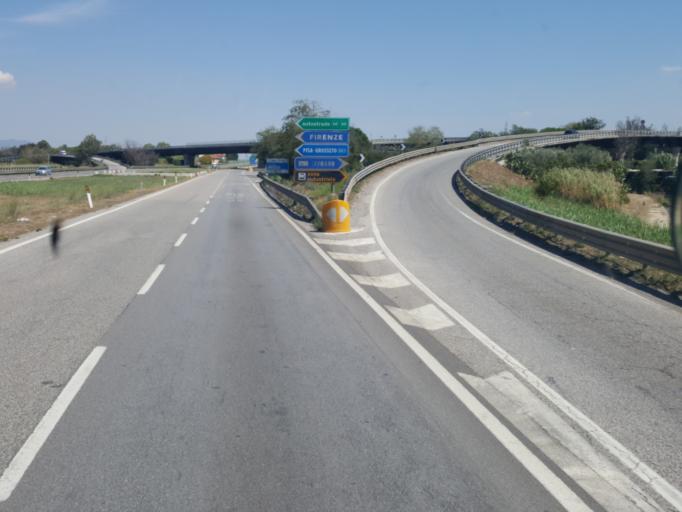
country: IT
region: Tuscany
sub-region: Provincia di Livorno
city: Livorno
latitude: 43.5950
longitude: 10.3462
